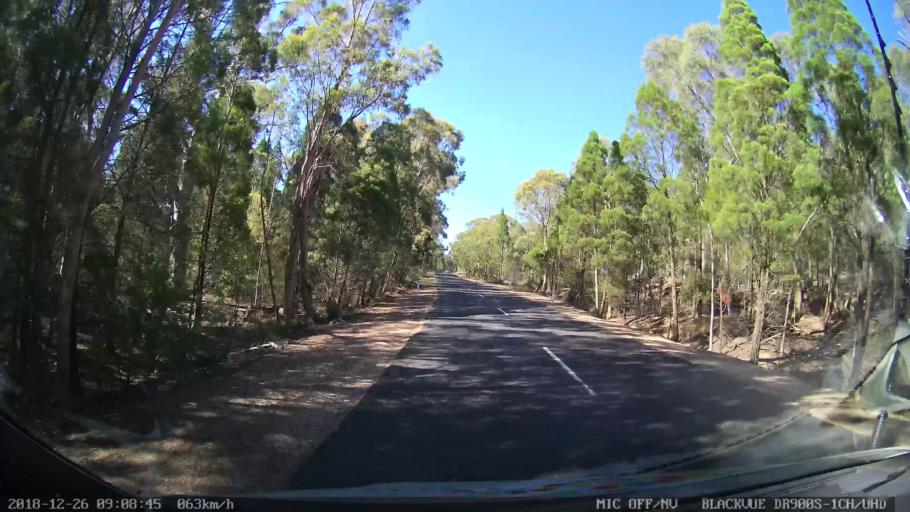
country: AU
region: New South Wales
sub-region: Mid-Western Regional
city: Kandos
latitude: -32.7183
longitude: 150.0000
